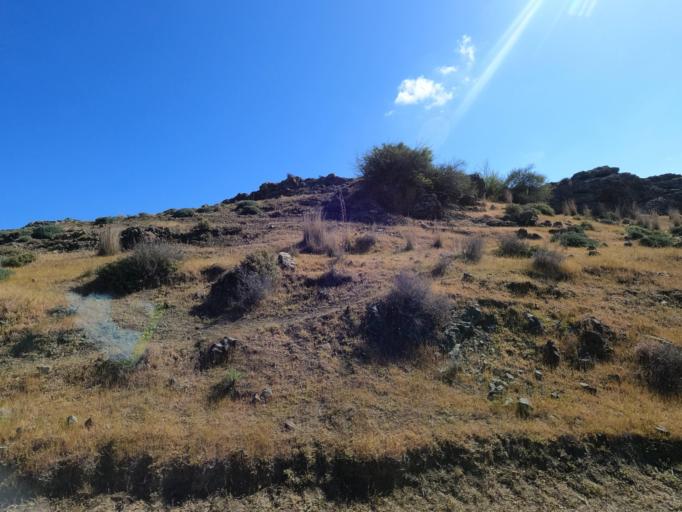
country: CY
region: Lefkosia
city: Peristerona
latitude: 35.0597
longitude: 33.0528
